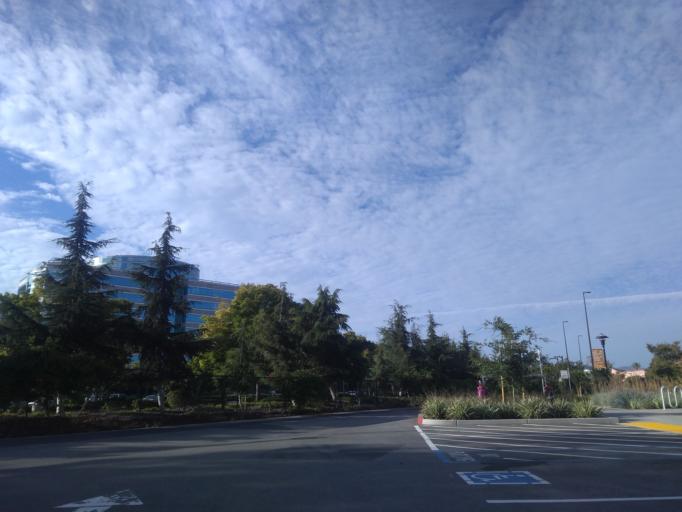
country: US
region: California
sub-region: Santa Clara County
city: Santa Clara
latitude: 37.3911
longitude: -121.9801
